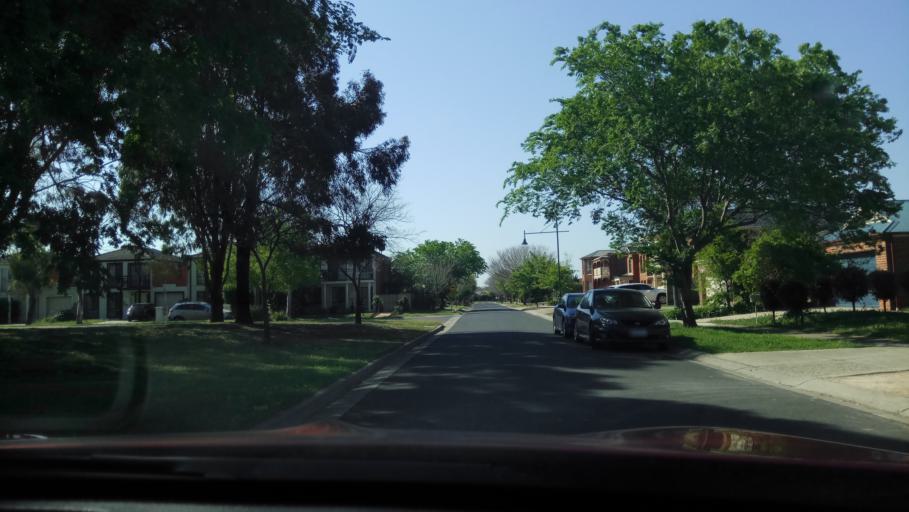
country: AU
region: Victoria
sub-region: Wyndham
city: Williams Landing
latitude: -37.8853
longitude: 144.7514
